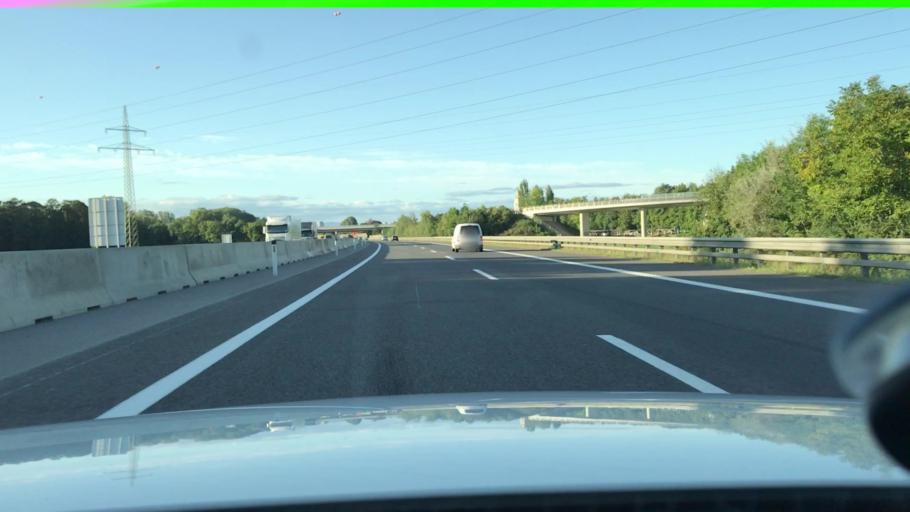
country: AT
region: Lower Austria
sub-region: Politischer Bezirk Sankt Polten
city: Herzogenburg
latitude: 48.2981
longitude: 15.7056
